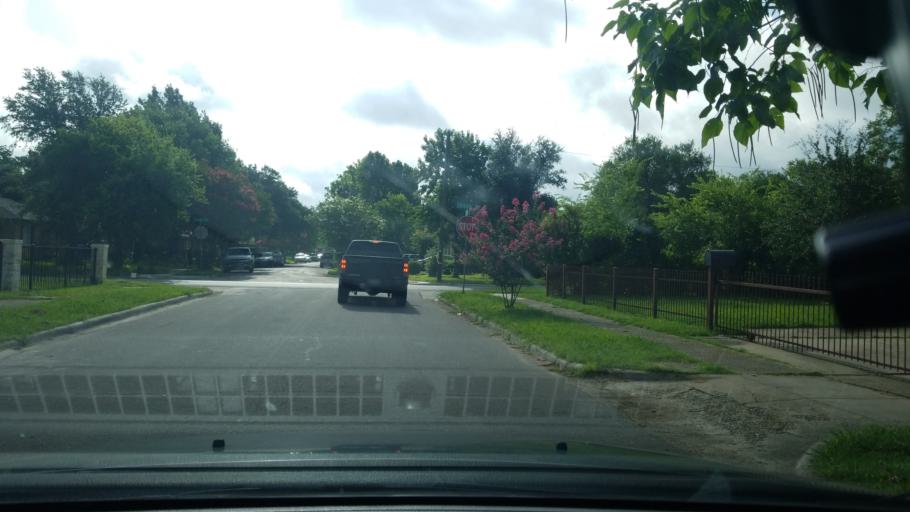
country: US
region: Texas
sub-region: Dallas County
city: Mesquite
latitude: 32.8197
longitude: -96.6689
